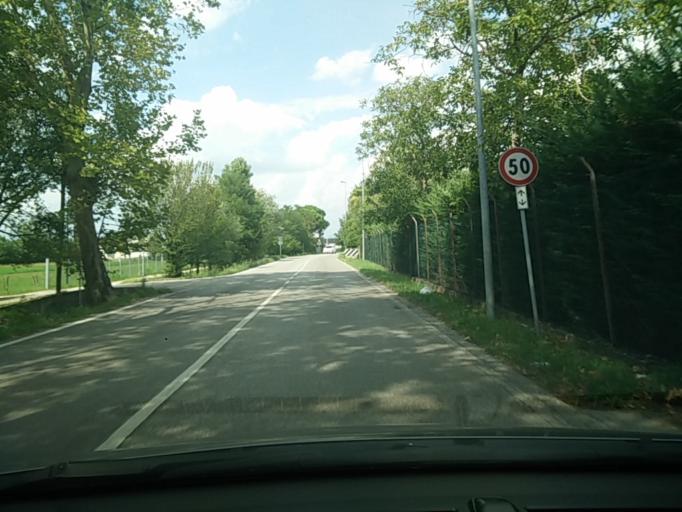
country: IT
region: Veneto
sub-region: Provincia di Treviso
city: Lancenigo-Villorba
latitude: 45.7294
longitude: 12.2400
